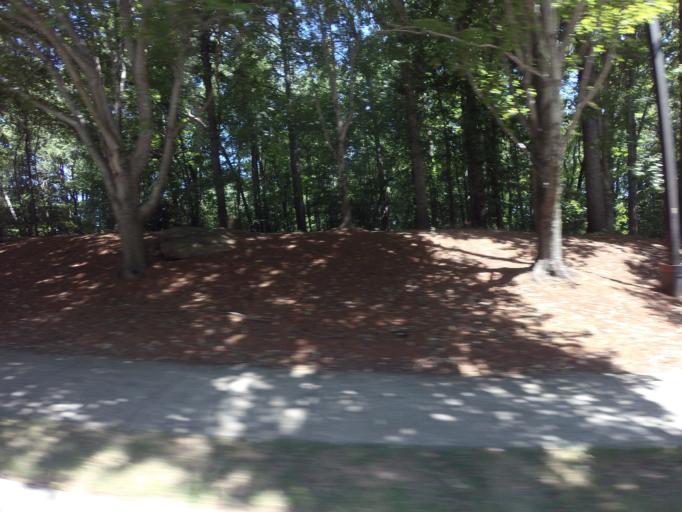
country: US
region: Georgia
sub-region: Fulton County
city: Johns Creek
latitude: 34.0601
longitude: -84.1632
